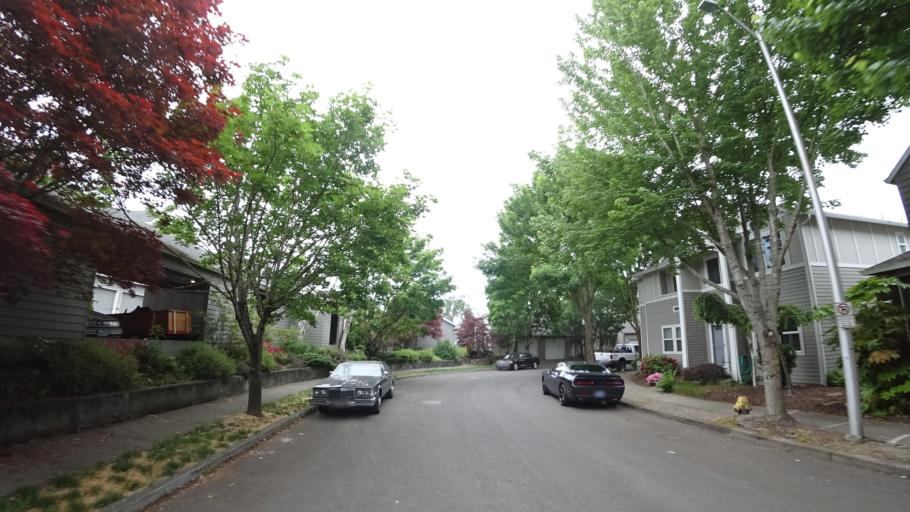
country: US
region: Washington
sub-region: Clark County
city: Vancouver
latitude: 45.6011
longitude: -122.6605
